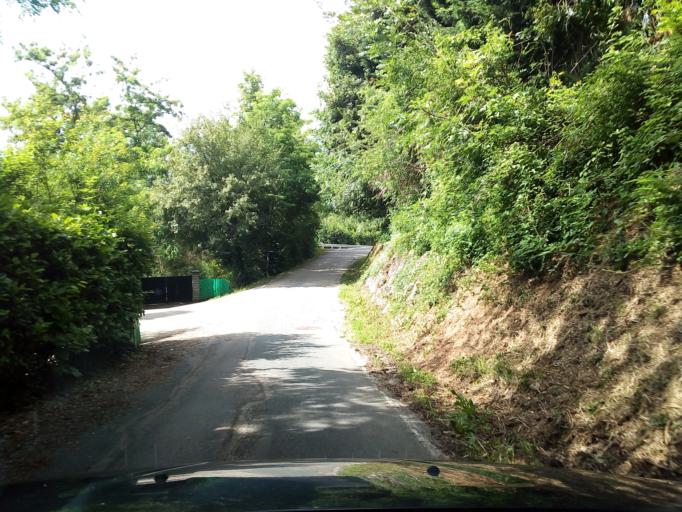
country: FR
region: Rhone-Alpes
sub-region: Departement de l'Isere
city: Saint-Martin-d'Heres
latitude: 45.1686
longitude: 5.7729
